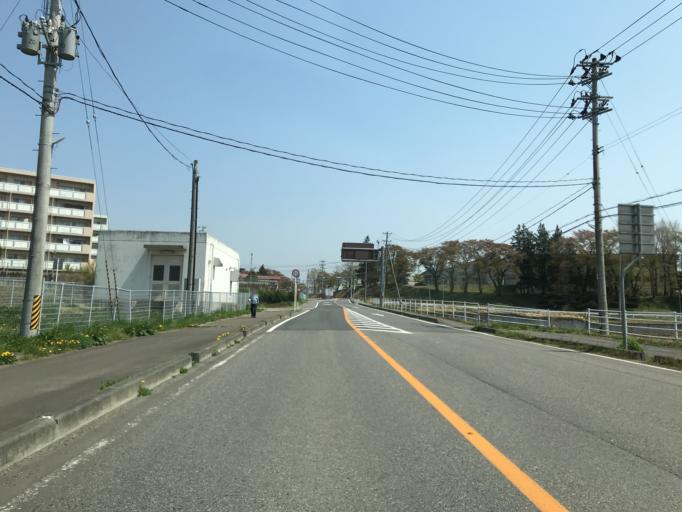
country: JP
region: Fukushima
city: Sukagawa
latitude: 37.1907
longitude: 140.3391
